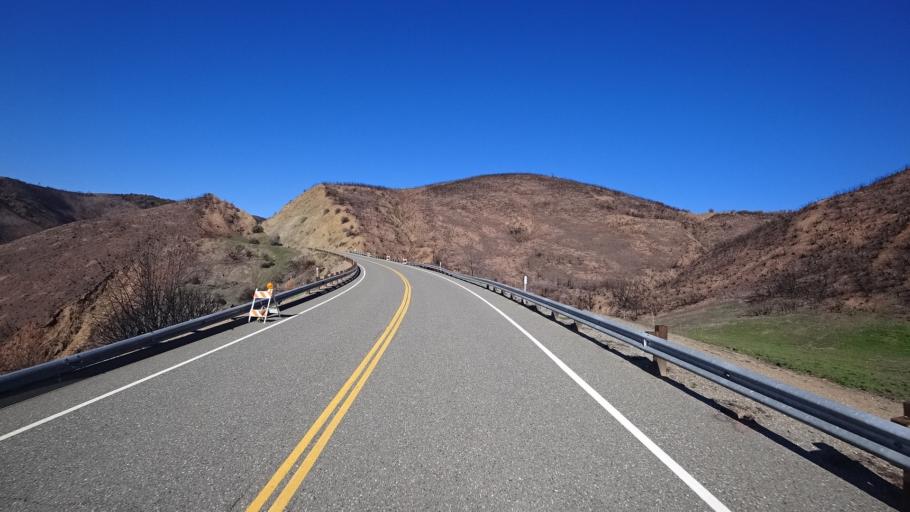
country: US
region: California
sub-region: Tehama County
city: Rancho Tehama Reserve
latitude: 39.6629
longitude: -122.6382
